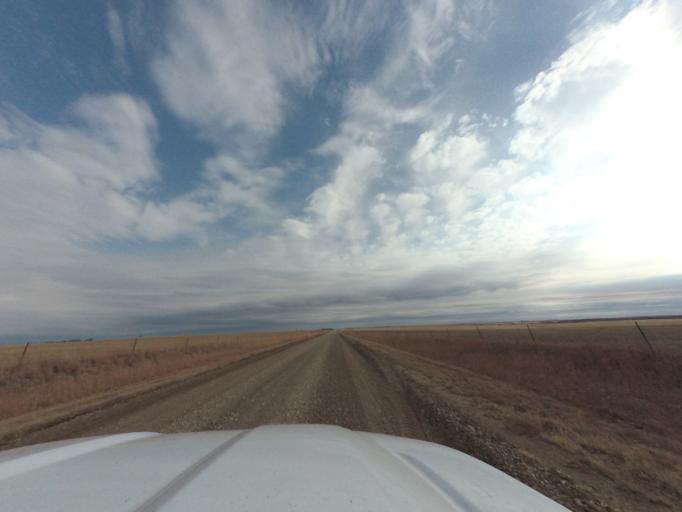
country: US
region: Kansas
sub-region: Chase County
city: Cottonwood Falls
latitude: 38.2170
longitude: -96.7211
